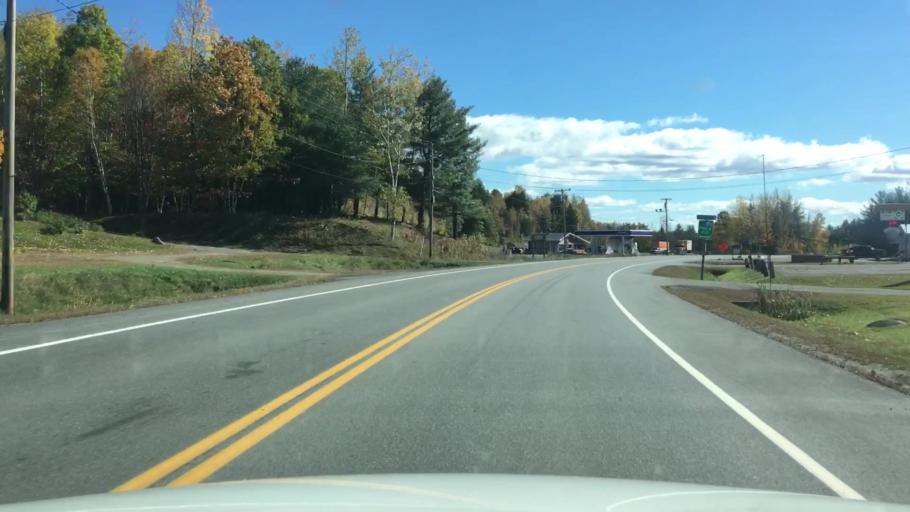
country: US
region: Maine
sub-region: Penobscot County
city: Medway
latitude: 45.6109
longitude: -68.5260
